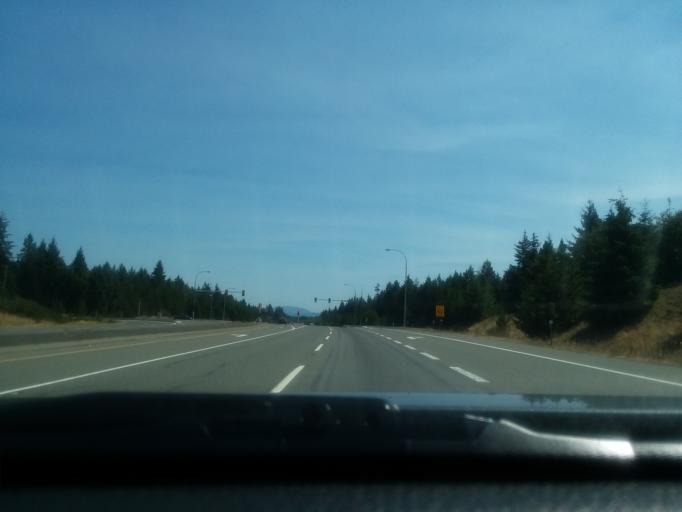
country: CA
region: British Columbia
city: Port Alberni
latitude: 49.3719
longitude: -124.6181
